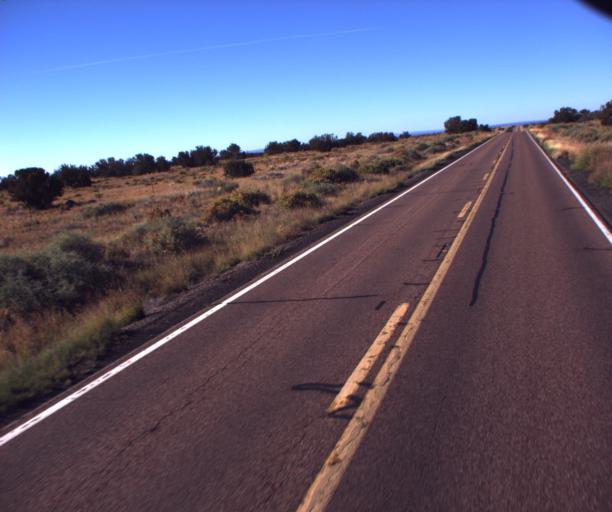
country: US
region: Arizona
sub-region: Navajo County
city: Snowflake
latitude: 34.6615
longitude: -110.3294
